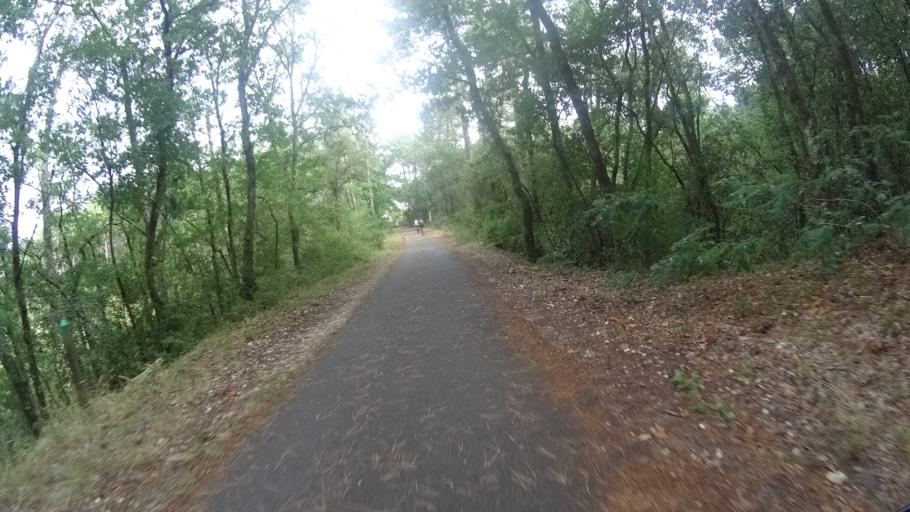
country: FR
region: Aquitaine
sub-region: Departement de la Gironde
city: Lacanau
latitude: 45.0049
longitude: -1.1385
